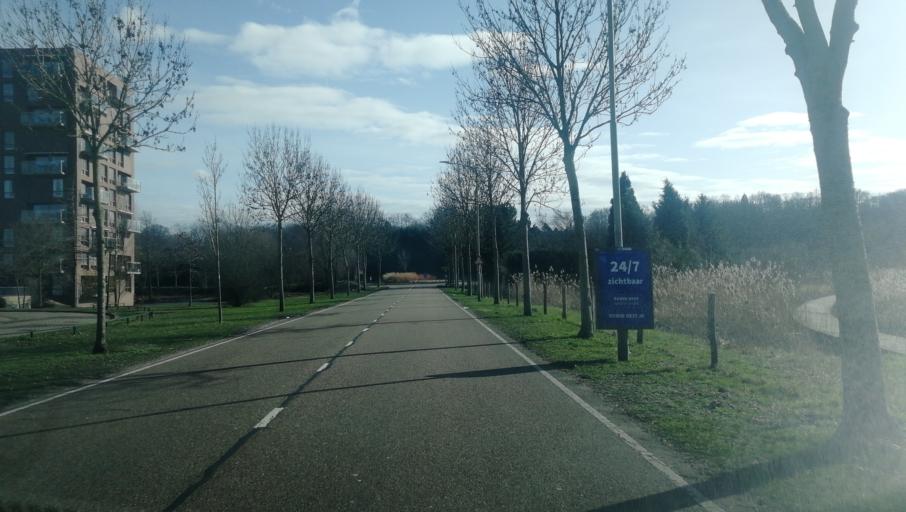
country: NL
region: Limburg
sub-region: Gemeente Venlo
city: Venlo
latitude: 51.3525
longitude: 6.1685
